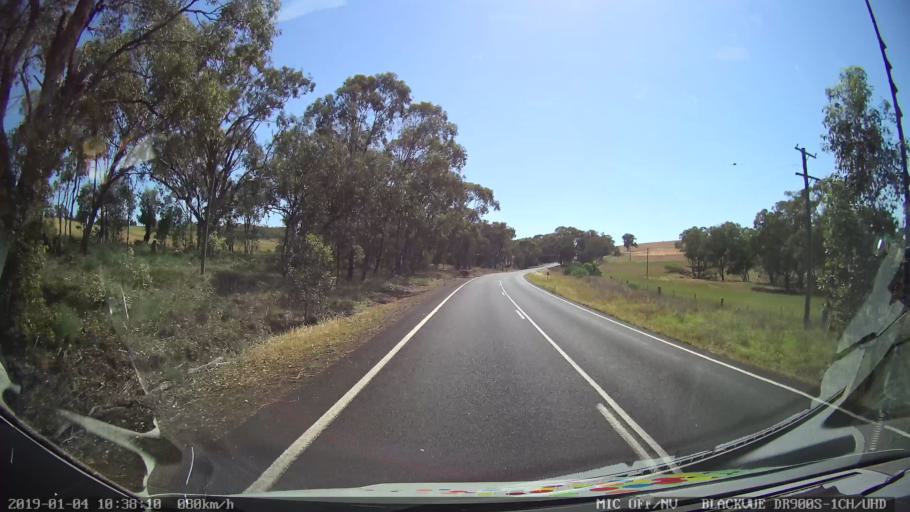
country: AU
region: New South Wales
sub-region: Cabonne
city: Molong
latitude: -33.2938
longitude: 148.7051
